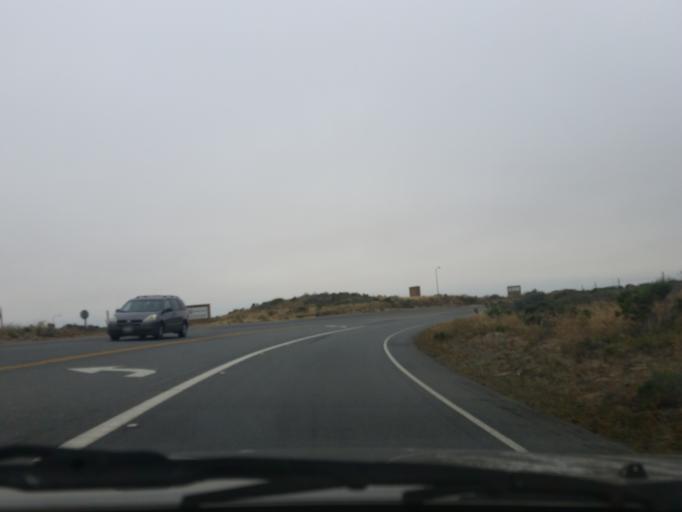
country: US
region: California
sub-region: San Luis Obispo County
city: Callender
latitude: 35.0473
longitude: -120.5909
